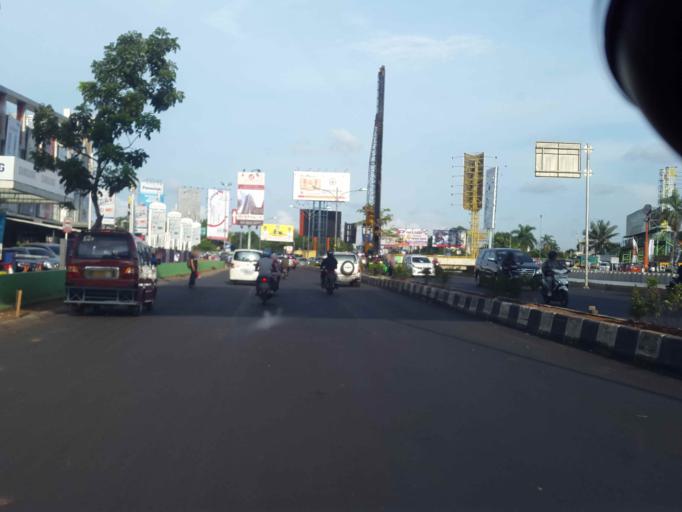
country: ID
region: West Java
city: Bekasi
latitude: -6.2475
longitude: 106.9906
